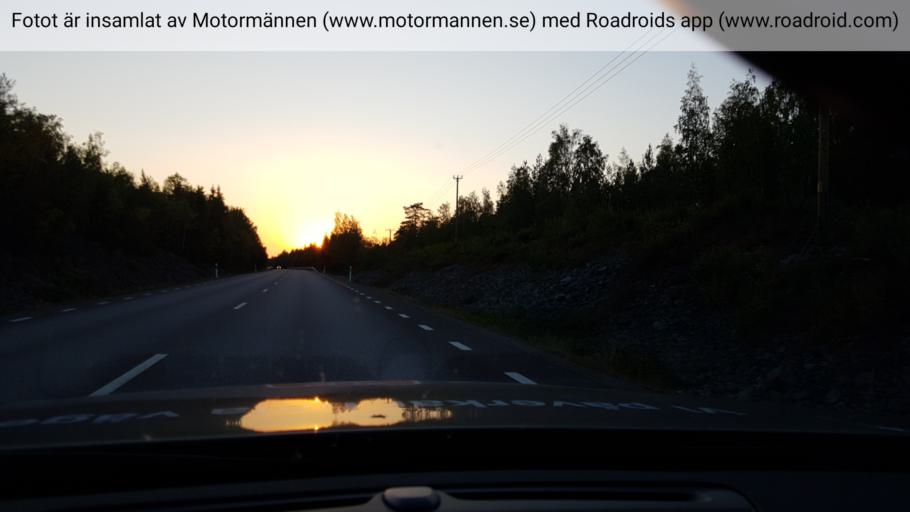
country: SE
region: Uppsala
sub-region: Osthammars Kommun
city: Bjorklinge
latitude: 59.9741
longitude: 17.3589
